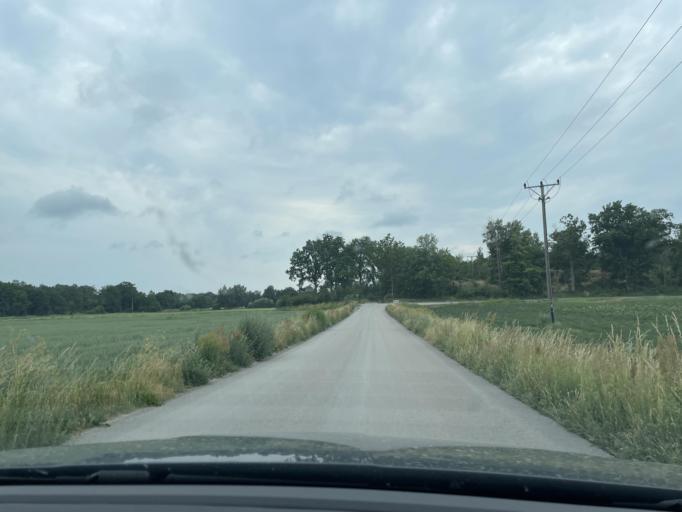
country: SE
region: Blekinge
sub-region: Karlshamns Kommun
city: Morrum
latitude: 56.1659
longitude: 14.7395
